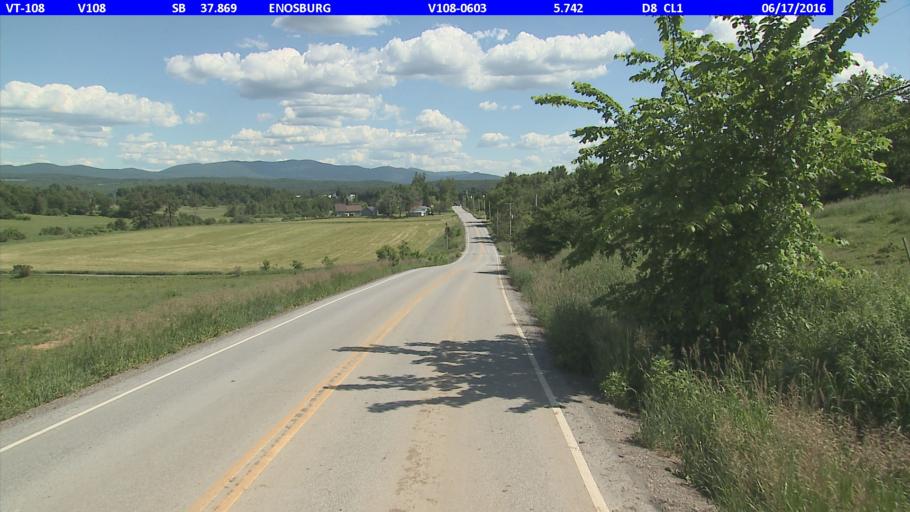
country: US
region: Vermont
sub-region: Franklin County
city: Enosburg Falls
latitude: 44.9228
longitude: -72.8084
